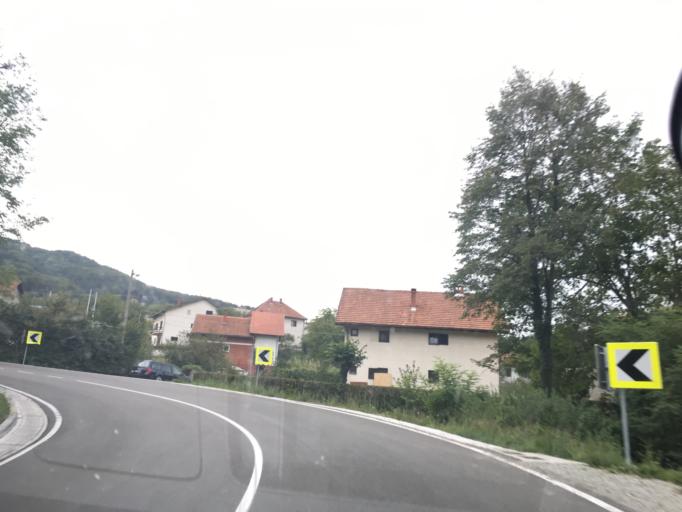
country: RS
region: Central Serbia
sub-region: Moravicki Okrug
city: Gornji Milanovac
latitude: 44.1436
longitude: 20.4971
